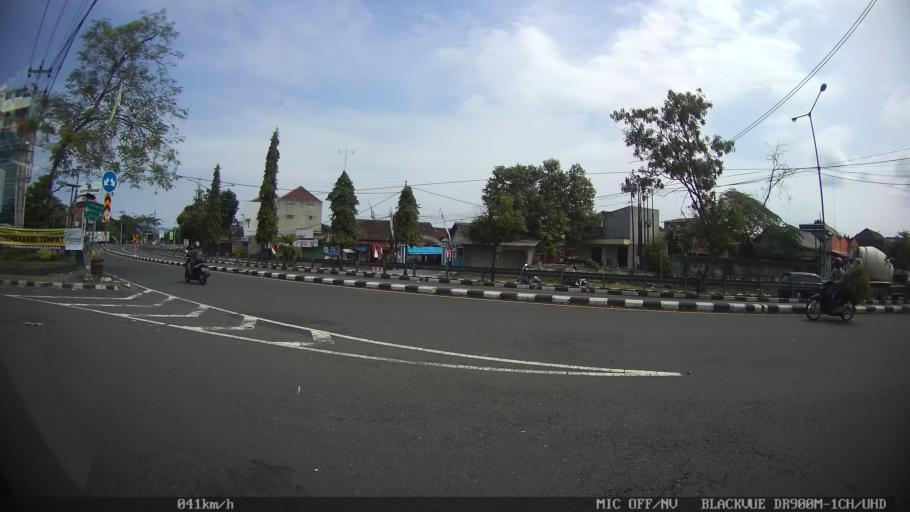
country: ID
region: Daerah Istimewa Yogyakarta
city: Depok
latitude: -7.7671
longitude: 110.4302
